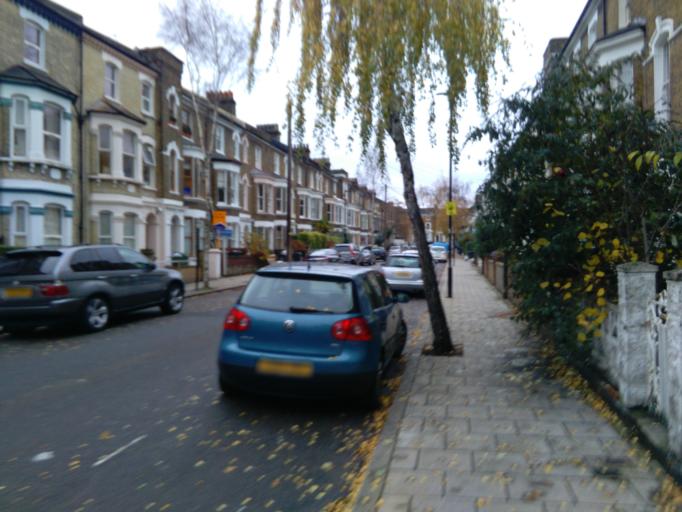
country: GB
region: England
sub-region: Greater London
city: Brixton
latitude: 51.4663
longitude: -0.1174
